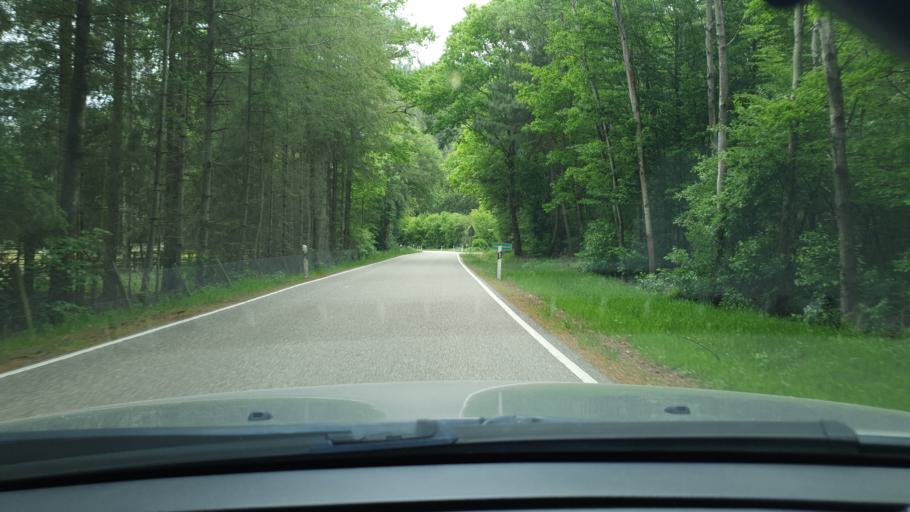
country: DE
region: Rheinland-Pfalz
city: Trippstadt
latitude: 49.3962
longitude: 7.7697
